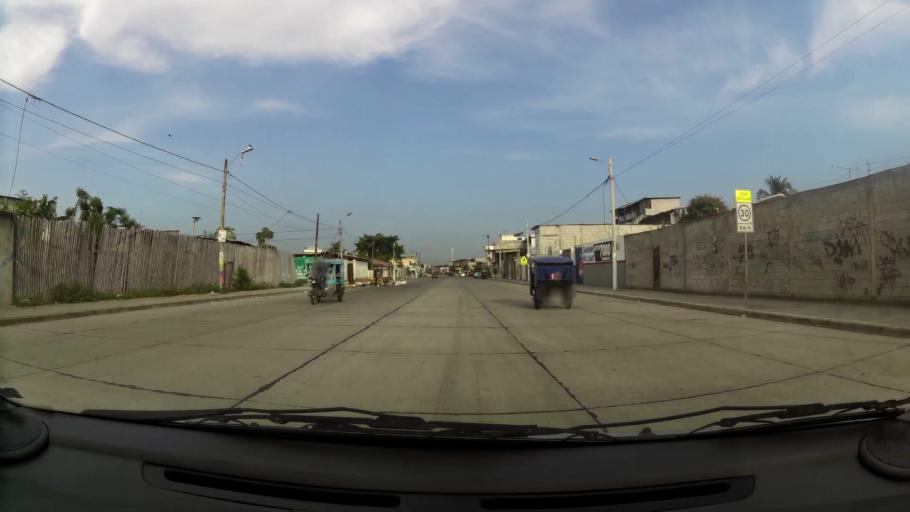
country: EC
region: Guayas
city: Eloy Alfaro
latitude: -2.0914
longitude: -79.9022
